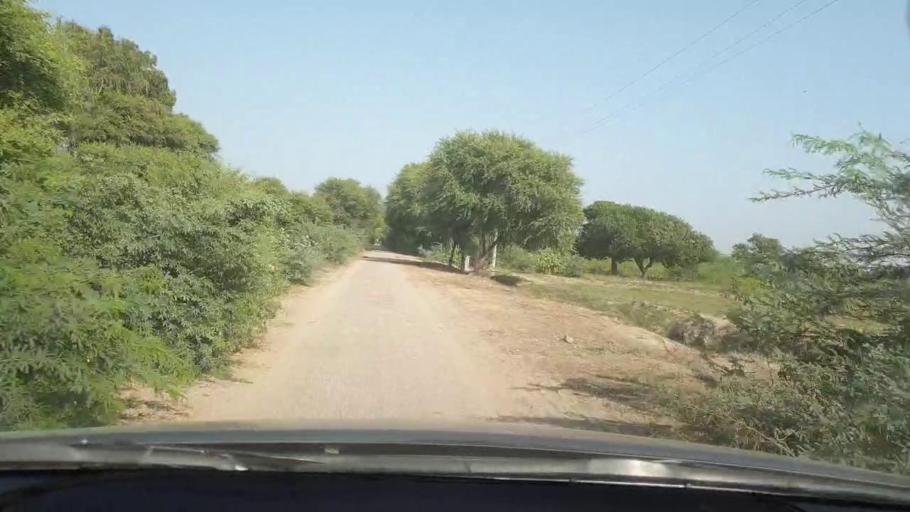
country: PK
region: Sindh
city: Naukot
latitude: 24.7666
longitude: 69.2512
